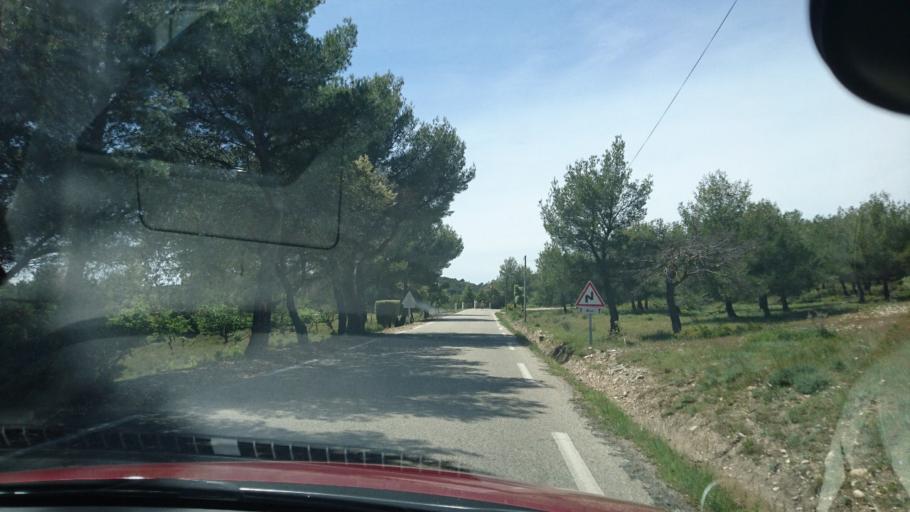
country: FR
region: Provence-Alpes-Cote d'Azur
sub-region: Departement du Vaucluse
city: Malaucene
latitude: 44.1380
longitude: 5.1430
